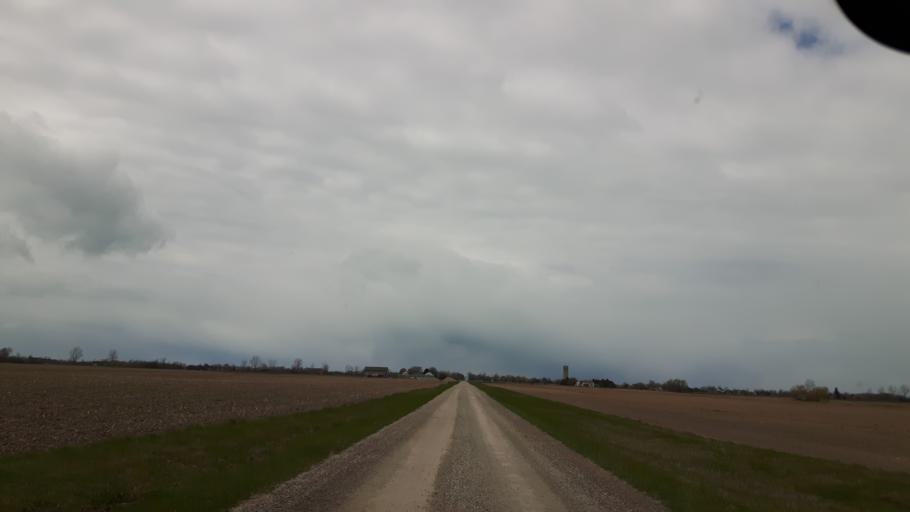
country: CA
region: Ontario
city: Bluewater
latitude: 43.4724
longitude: -81.6870
